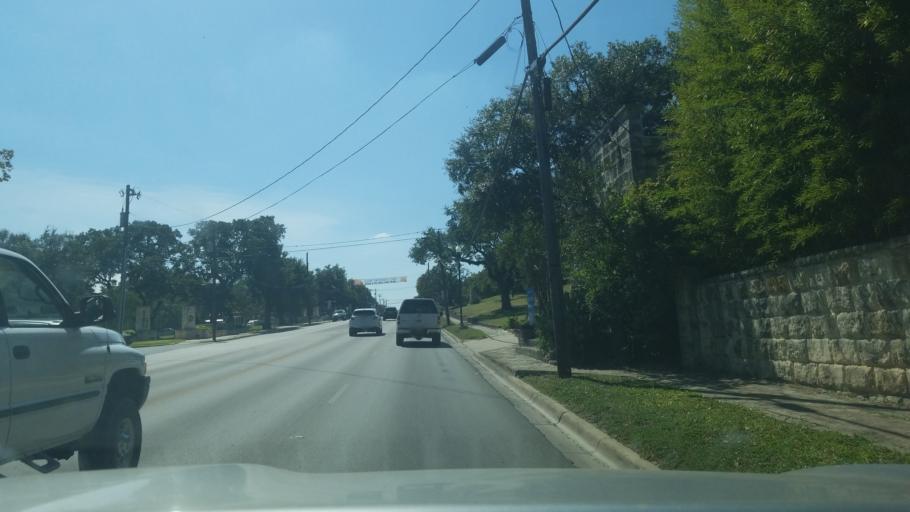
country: US
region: Texas
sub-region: Kendall County
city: Boerne
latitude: 29.7869
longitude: -98.7291
